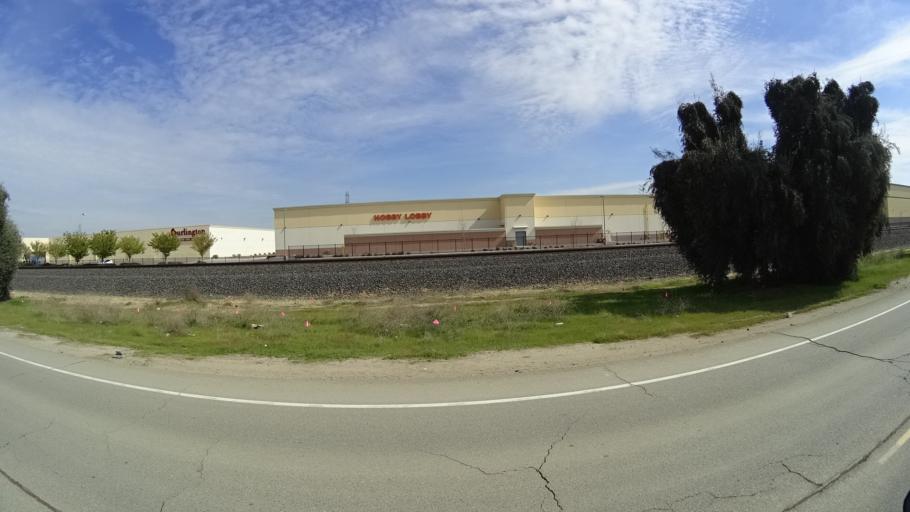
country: US
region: California
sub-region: Fresno County
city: Biola
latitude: 36.8304
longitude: -119.9100
